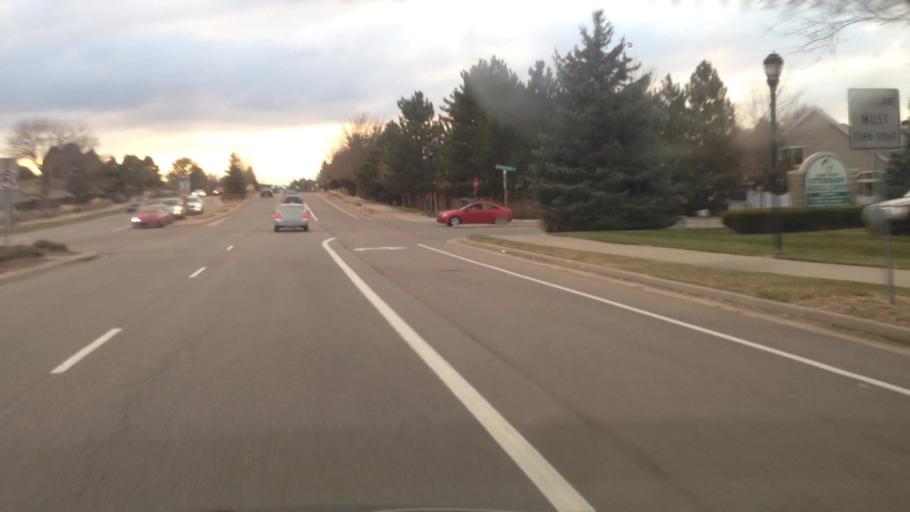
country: US
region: Colorado
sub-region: Douglas County
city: Carriage Club
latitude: 39.5364
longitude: -104.8889
